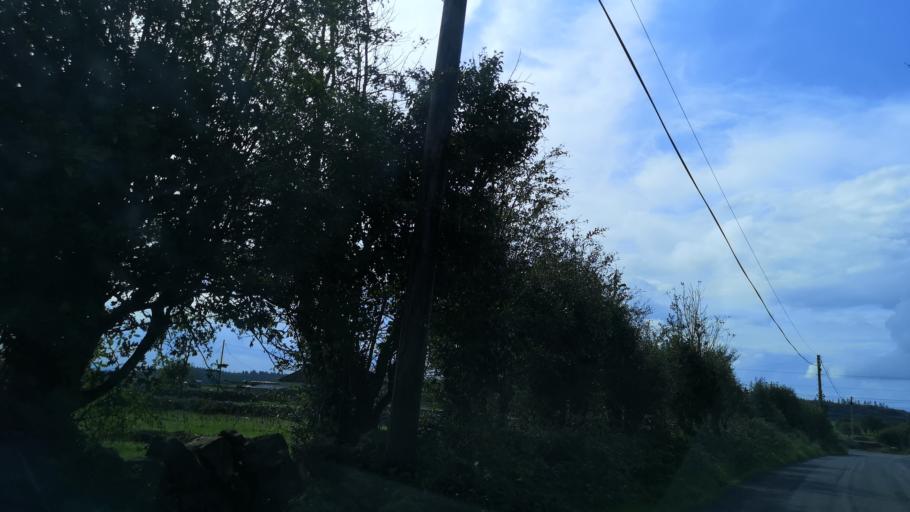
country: IE
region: Connaught
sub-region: County Galway
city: Athenry
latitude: 53.3031
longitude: -8.8133
